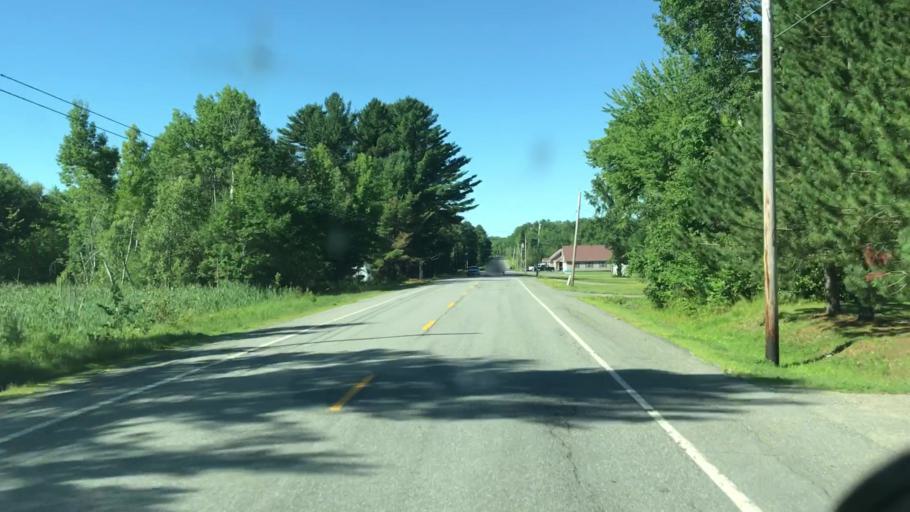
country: US
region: Maine
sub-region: Penobscot County
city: Howland
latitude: 45.2790
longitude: -68.6319
